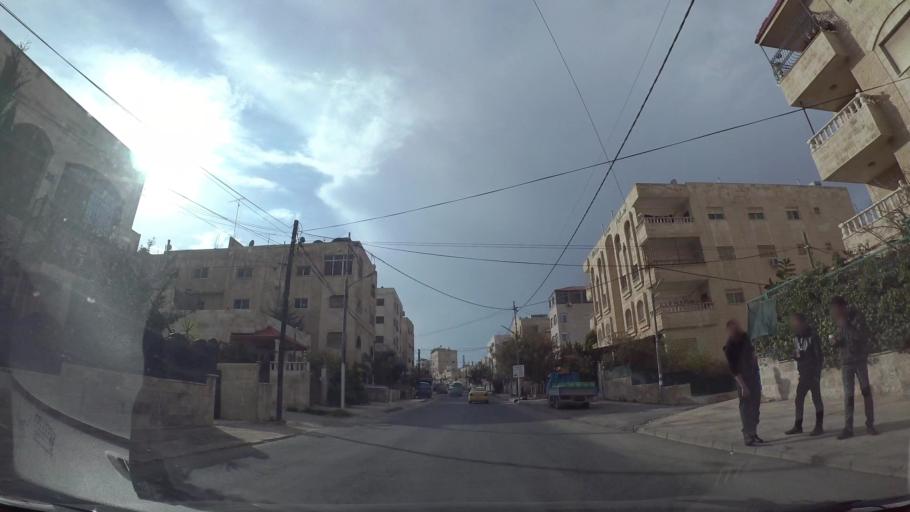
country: JO
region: Amman
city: Amman
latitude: 32.0008
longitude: 35.9464
